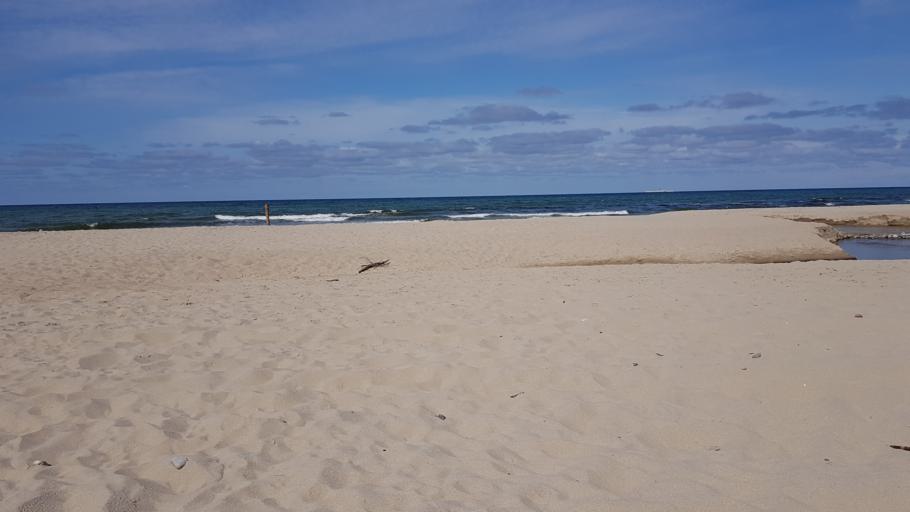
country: RU
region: Kaliningrad
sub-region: Gorod Kaliningrad
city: Pionerskiy
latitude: 54.9411
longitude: 20.3094
